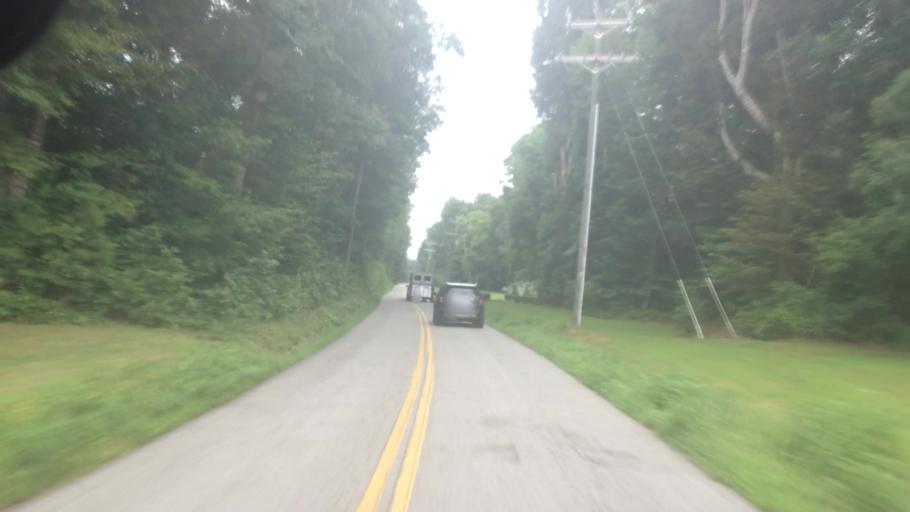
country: US
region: Virginia
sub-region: King William County
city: West Point
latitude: 37.5669
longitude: -76.7072
